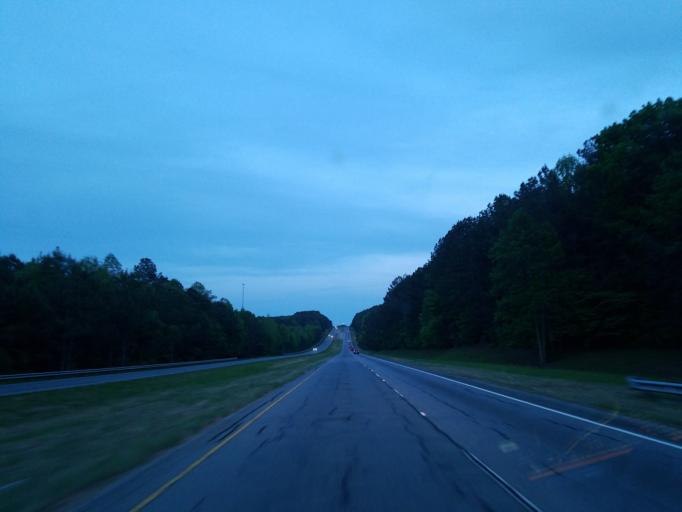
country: US
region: Georgia
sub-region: Pickens County
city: Jasper
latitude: 34.4979
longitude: -84.4981
